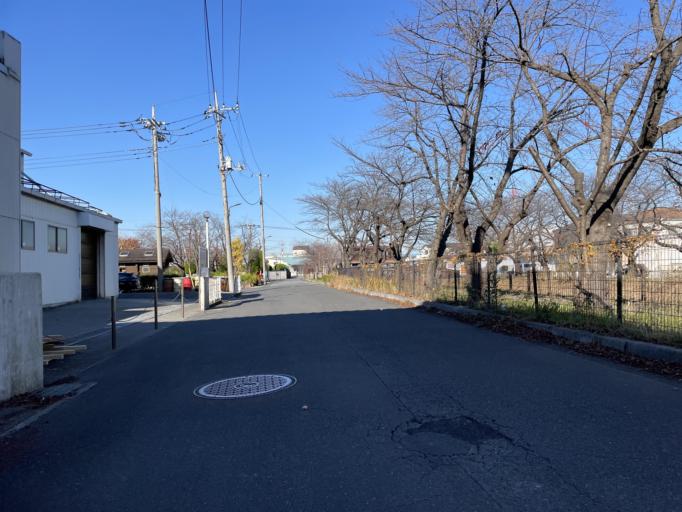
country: JP
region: Saitama
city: Yashio-shi
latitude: 35.8442
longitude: 139.8260
